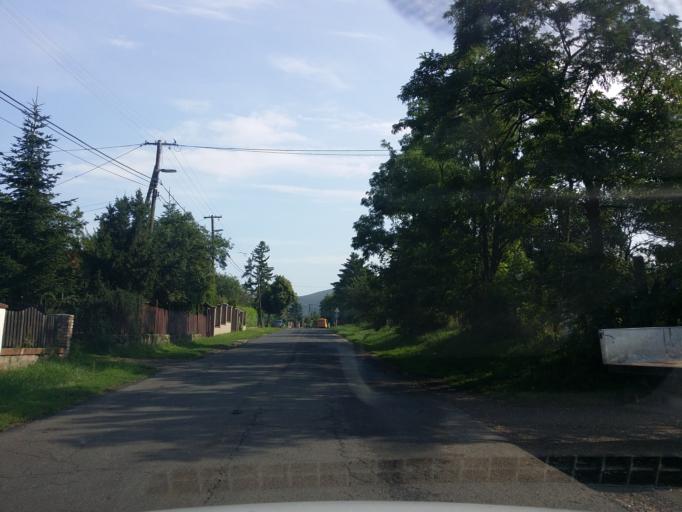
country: HU
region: Borsod-Abauj-Zemplen
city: Gonc
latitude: 48.3899
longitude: 21.2821
